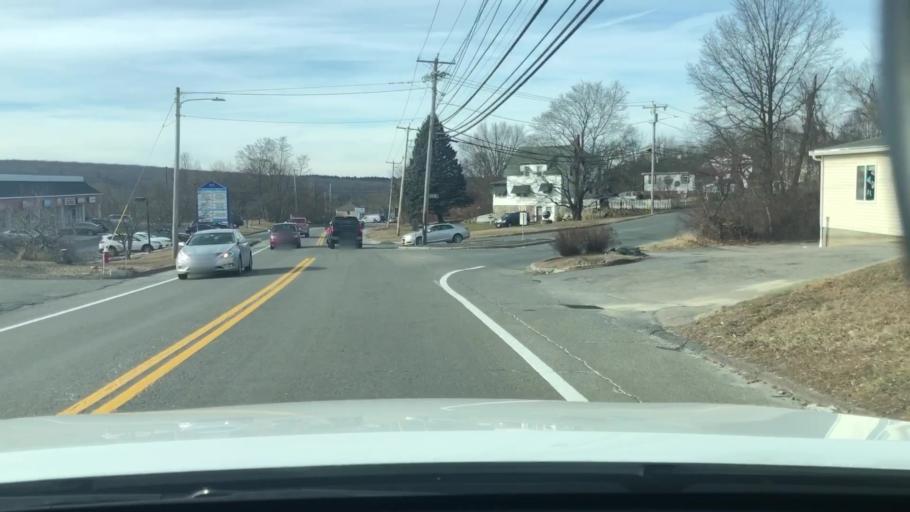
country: US
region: Massachusetts
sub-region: Worcester County
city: Hopedale
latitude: 42.1425
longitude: -71.5438
